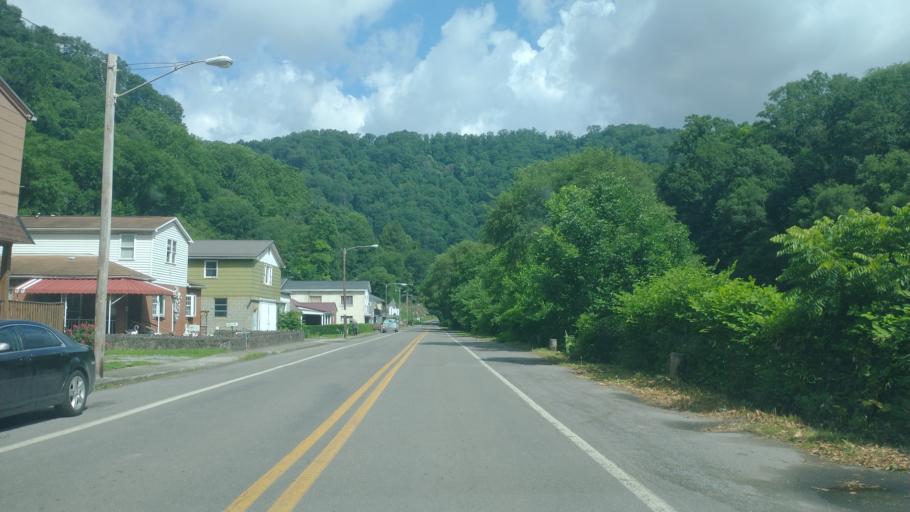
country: US
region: West Virginia
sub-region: McDowell County
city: Welch
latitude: 37.4178
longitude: -81.4381
